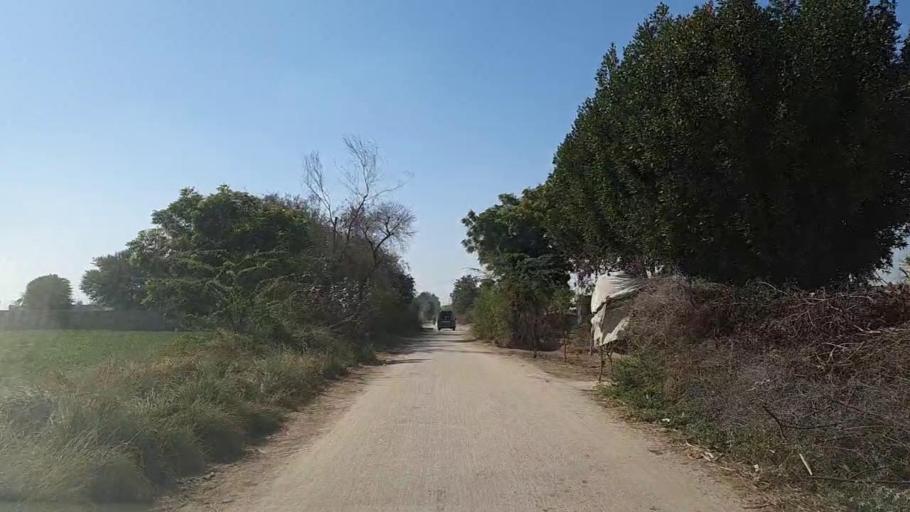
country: PK
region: Sindh
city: Nawabshah
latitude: 26.2446
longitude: 68.4354
